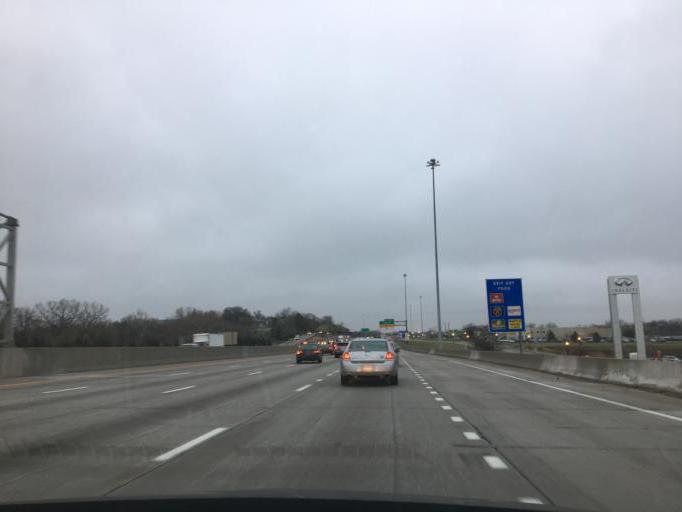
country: US
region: Kansas
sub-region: Johnson County
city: Merriam
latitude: 39.0039
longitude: -94.6945
